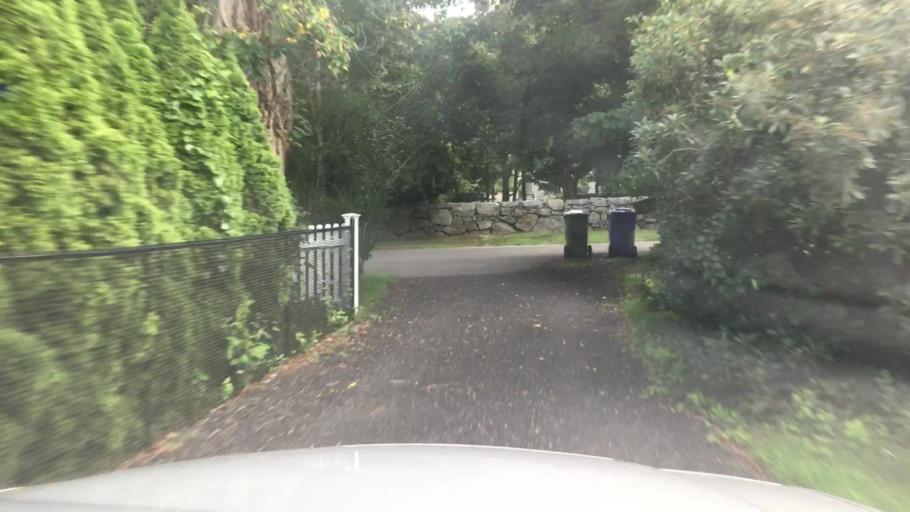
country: US
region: Connecticut
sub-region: Middlesex County
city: Essex Village
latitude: 41.3509
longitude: -72.3952
